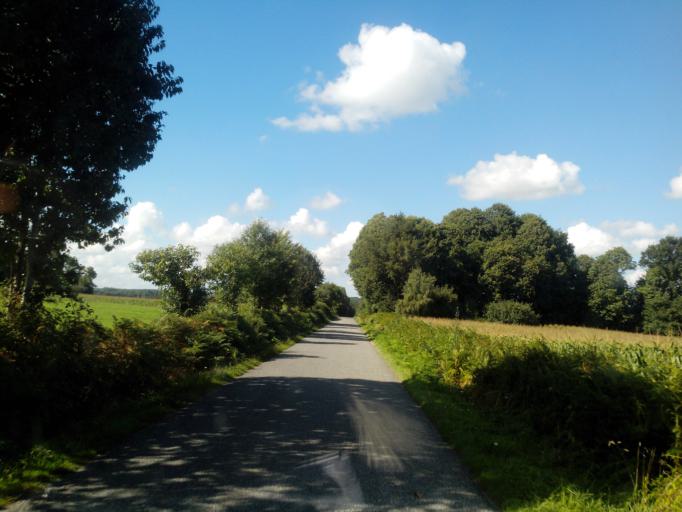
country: FR
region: Brittany
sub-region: Departement des Cotes-d'Armor
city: Merdrignac
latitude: 48.1657
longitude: -2.4181
